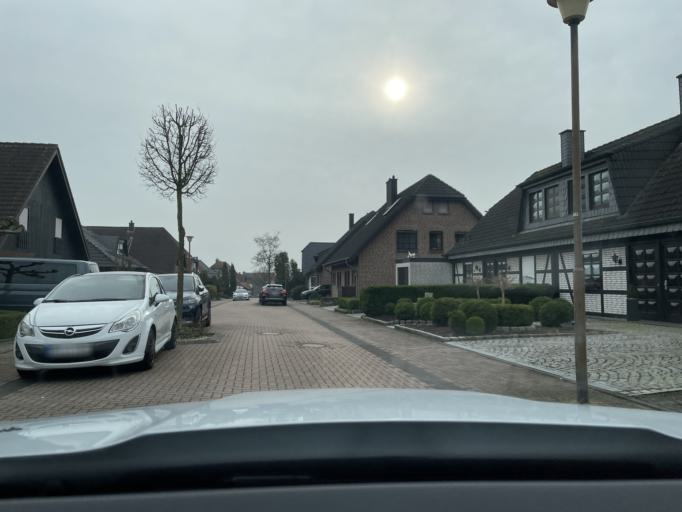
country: DE
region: North Rhine-Westphalia
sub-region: Regierungsbezirk Dusseldorf
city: Wachtendonk
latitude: 51.4033
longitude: 6.3075
